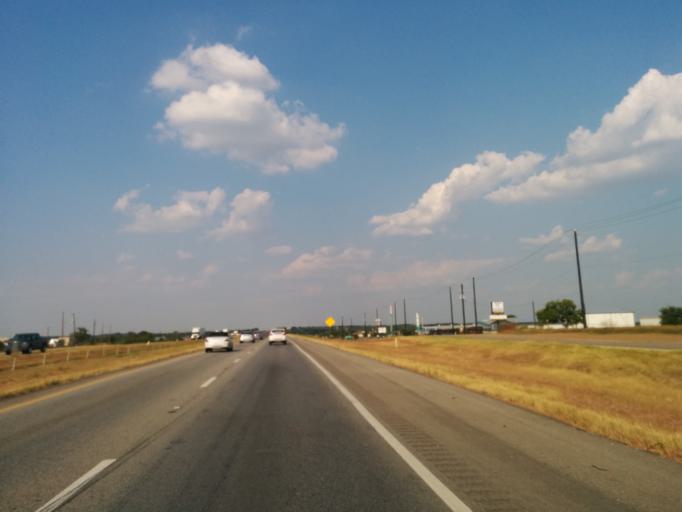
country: US
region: Texas
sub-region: Bexar County
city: Converse
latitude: 29.4758
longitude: -98.2588
